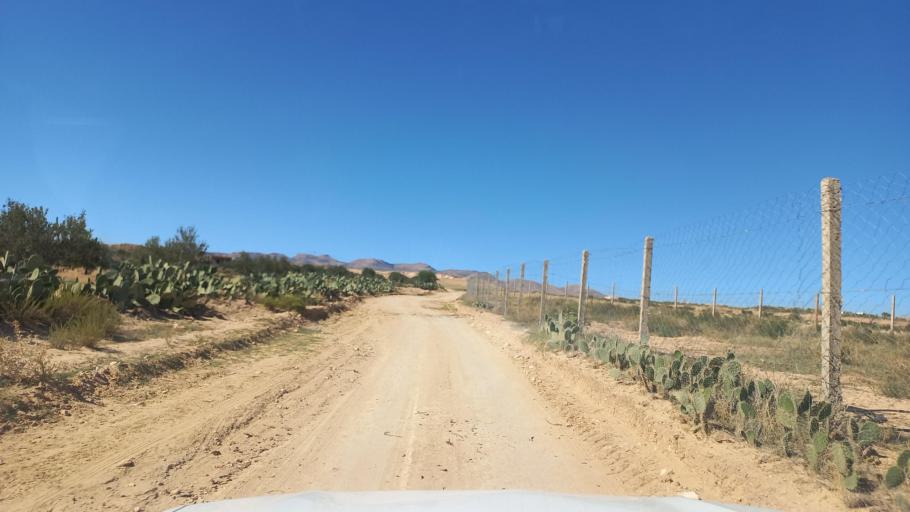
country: TN
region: Al Qasrayn
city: Sbiba
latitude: 35.3755
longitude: 9.0921
